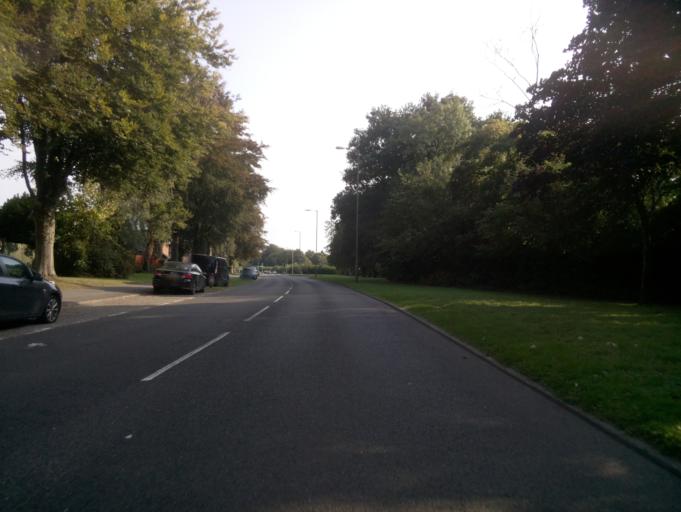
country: GB
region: Wales
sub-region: Torfaen County Borough
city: Cwmbran
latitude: 51.6437
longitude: -3.0066
